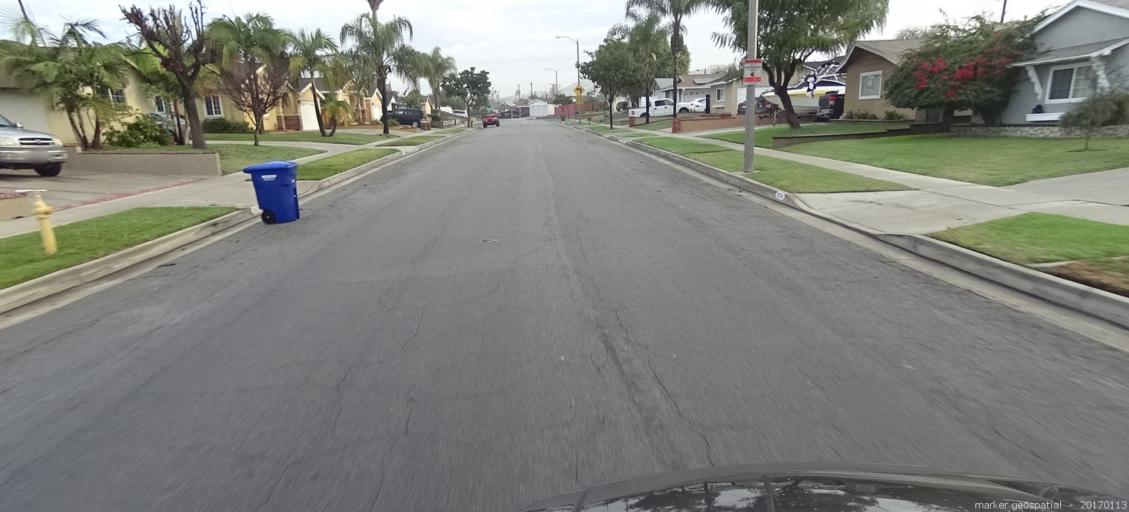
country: US
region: California
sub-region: Orange County
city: Buena Park
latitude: 33.8894
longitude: -117.9953
